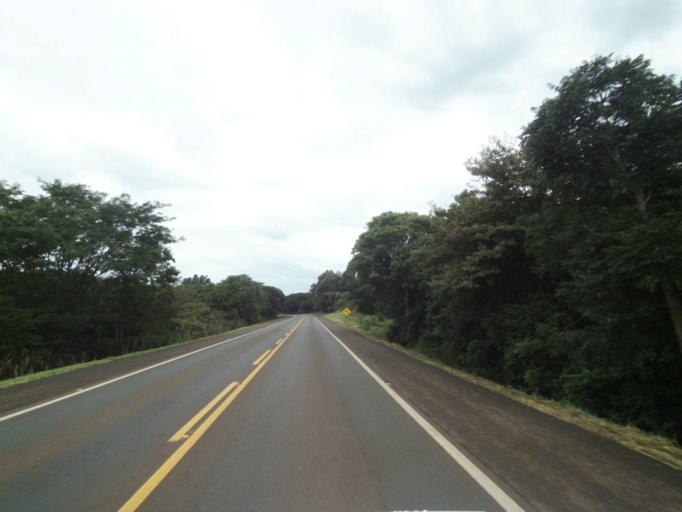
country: BR
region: Parana
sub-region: Guaraniacu
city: Guaraniacu
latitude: -25.1113
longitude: -52.8469
